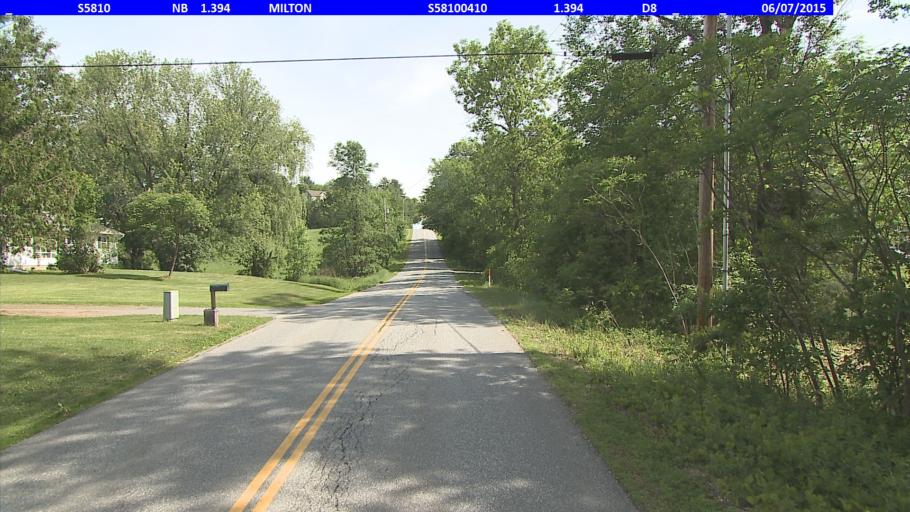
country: US
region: Vermont
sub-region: Chittenden County
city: Milton
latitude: 44.6014
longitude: -73.1270
